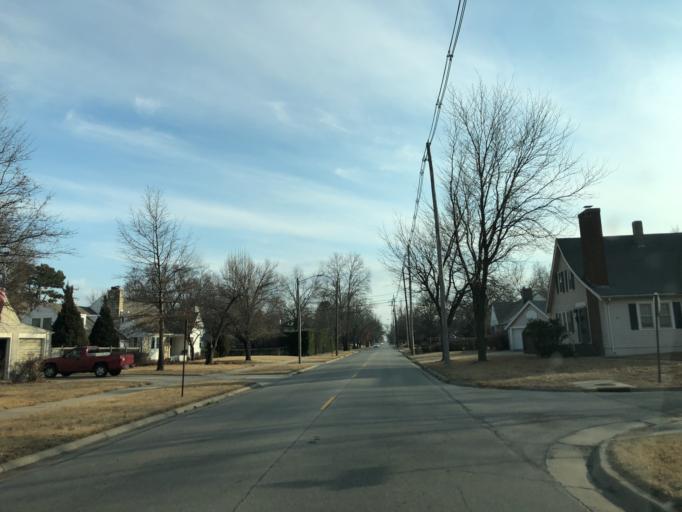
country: US
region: Kansas
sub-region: Reno County
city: Hutchinson
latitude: 38.0778
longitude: -97.9355
